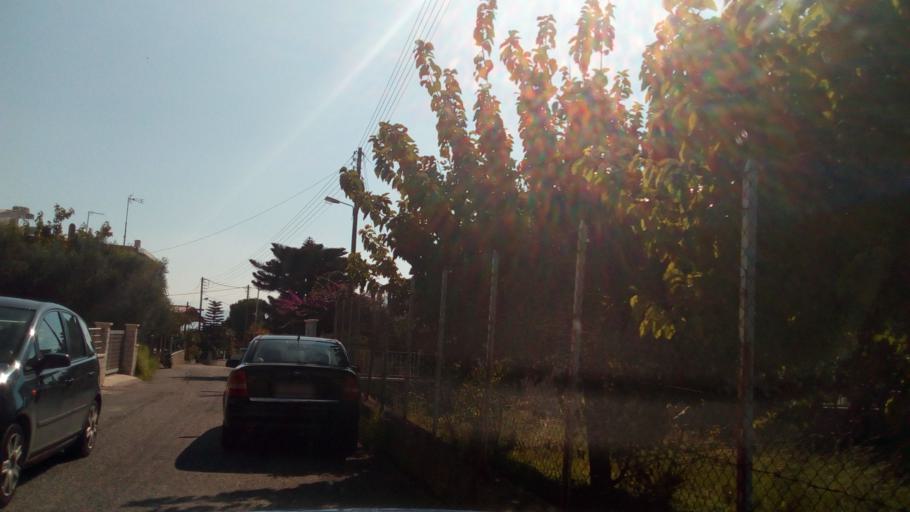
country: GR
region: West Greece
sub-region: Nomos Aitolias kai Akarnanias
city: Nafpaktos
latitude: 38.4167
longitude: 21.8736
